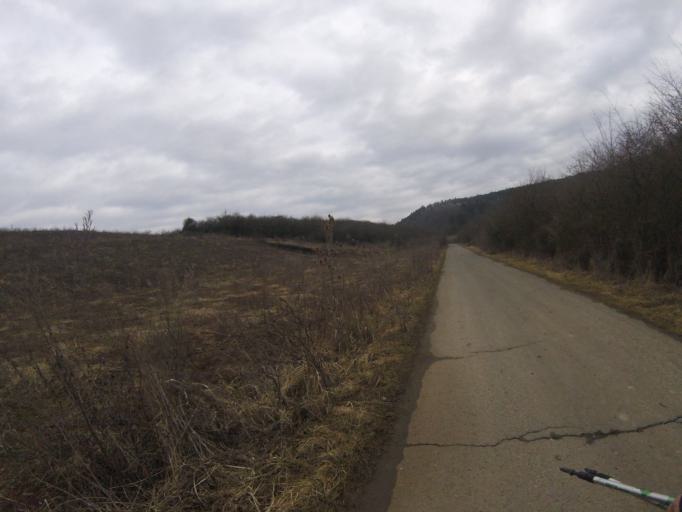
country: HU
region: Heves
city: Egerszalok
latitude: 47.8395
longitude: 20.3376
